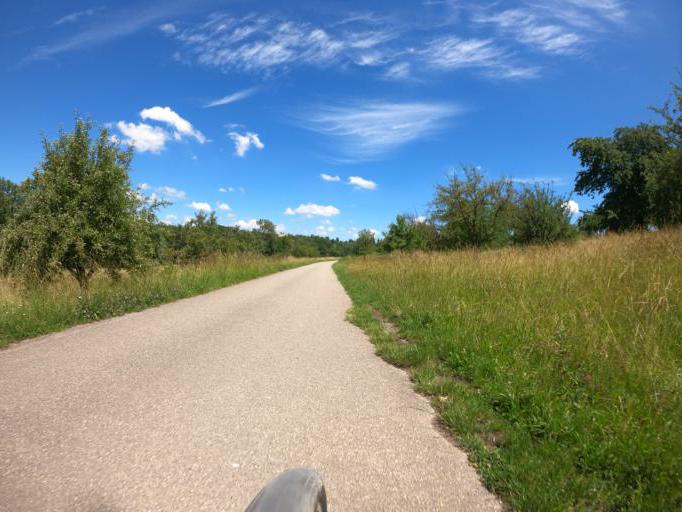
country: DE
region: Baden-Wuerttemberg
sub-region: Regierungsbezirk Stuttgart
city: Bietigheim-Bissingen
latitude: 48.9401
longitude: 9.0838
